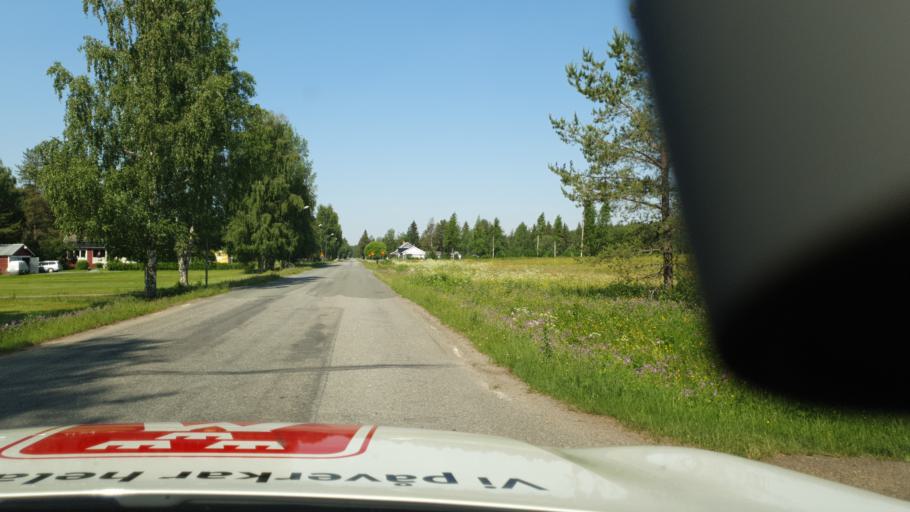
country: SE
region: Vaesterbotten
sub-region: Skelleftea Kommun
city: Langsele
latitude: 64.9483
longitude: 19.9328
